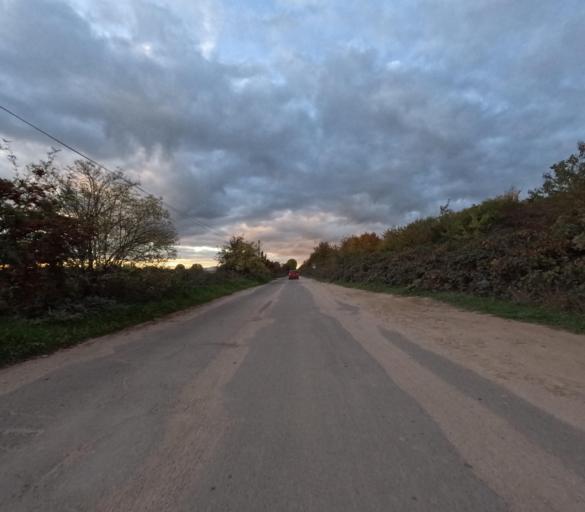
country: DE
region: Saxony
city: Borsdorf
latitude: 51.3093
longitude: 12.5286
